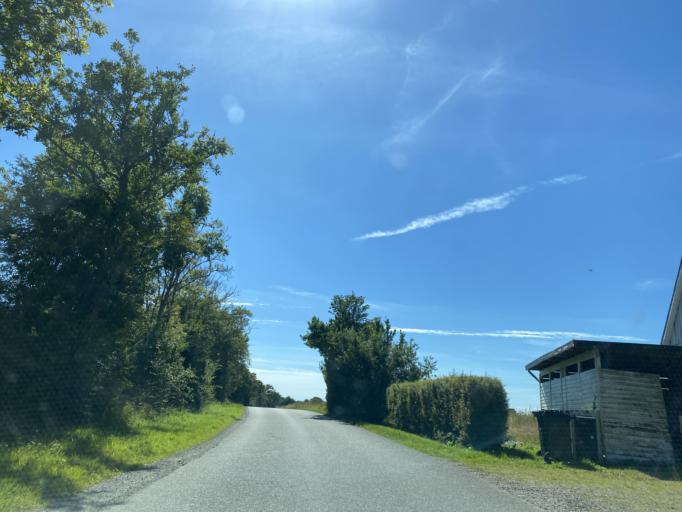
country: DK
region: South Denmark
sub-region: Kolding Kommune
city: Christiansfeld
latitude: 55.3812
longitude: 9.5027
